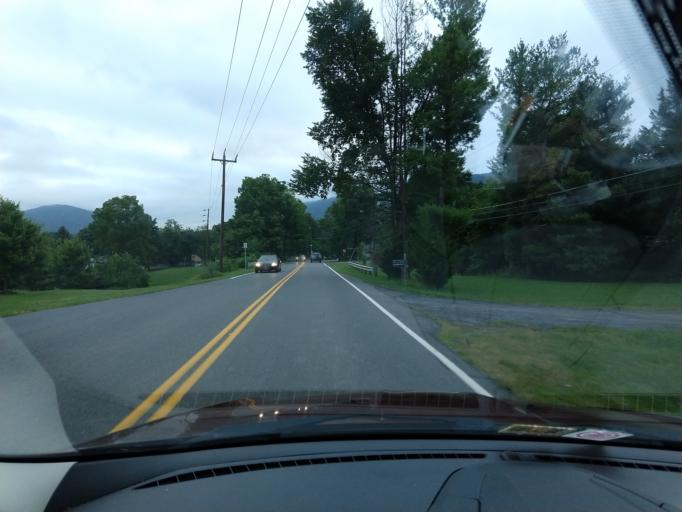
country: US
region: Virginia
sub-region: City of Covington
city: Fairlawn
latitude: 37.7522
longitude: -79.9940
